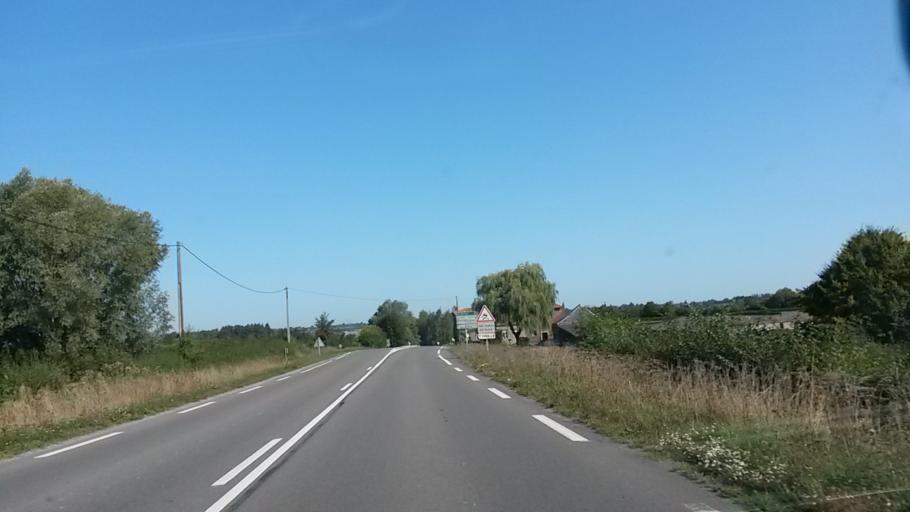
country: FR
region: Picardie
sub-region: Departement de l'Aisne
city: La Flamengrie
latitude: 50.0477
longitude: 3.9272
